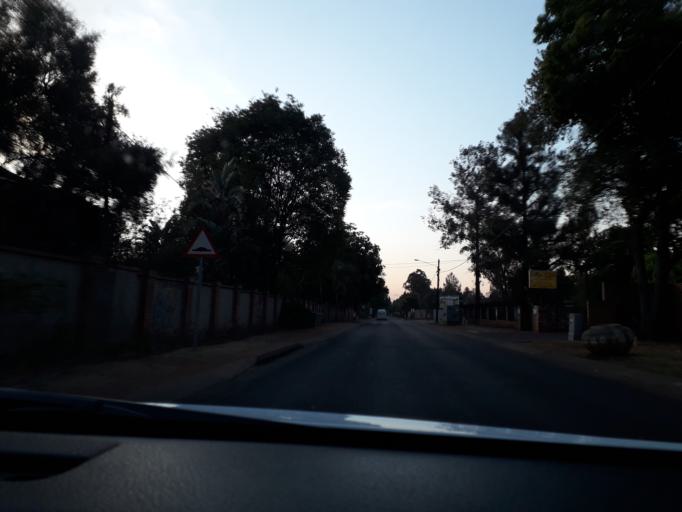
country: ZA
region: Gauteng
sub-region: City of Tshwane Metropolitan Municipality
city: Centurion
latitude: -25.8455
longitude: 28.1784
